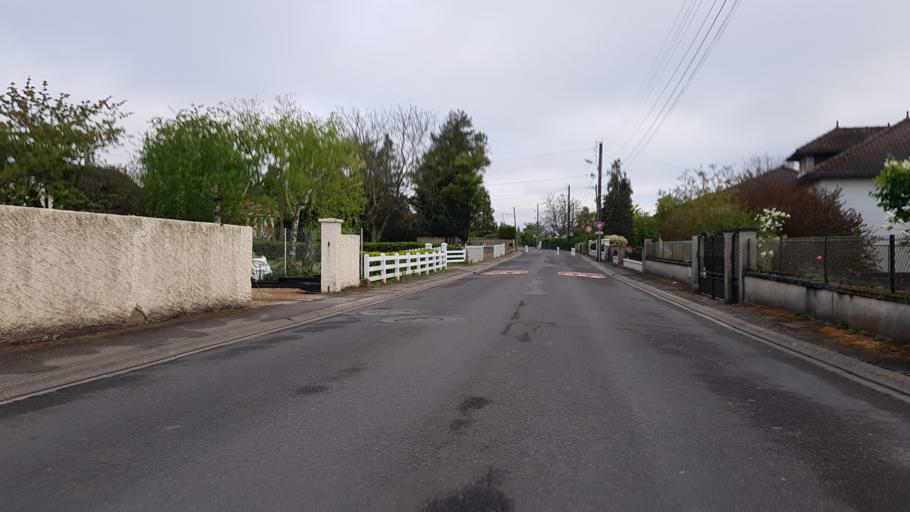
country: FR
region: Poitou-Charentes
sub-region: Departement de la Vienne
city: Jaunay-Clan
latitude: 46.6732
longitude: 0.3740
